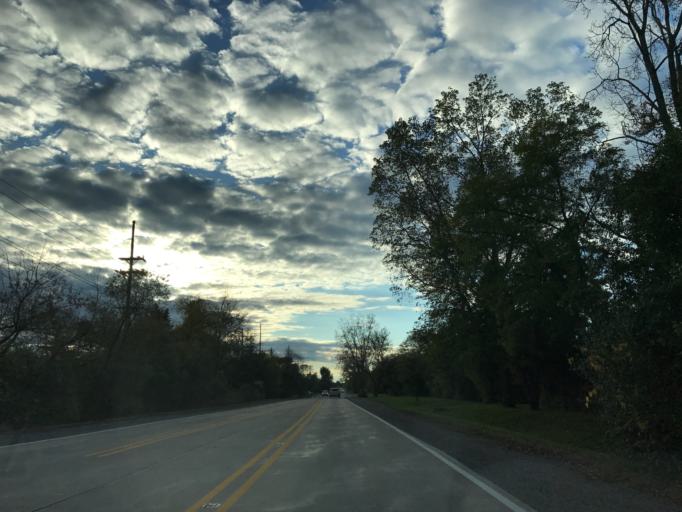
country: US
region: Michigan
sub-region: Oakland County
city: Franklin
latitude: 42.4856
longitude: -83.3198
